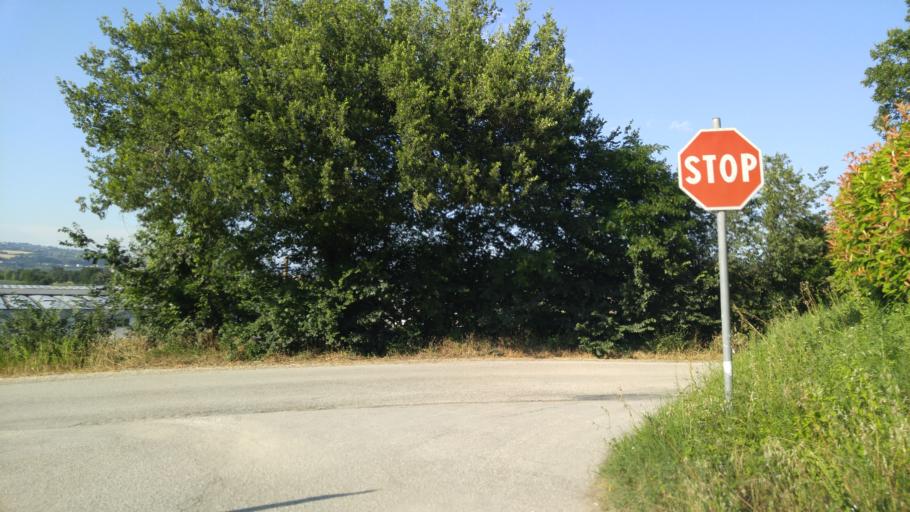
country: IT
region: The Marches
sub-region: Provincia di Pesaro e Urbino
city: Sant'Ippolito
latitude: 43.7022
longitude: 12.8794
